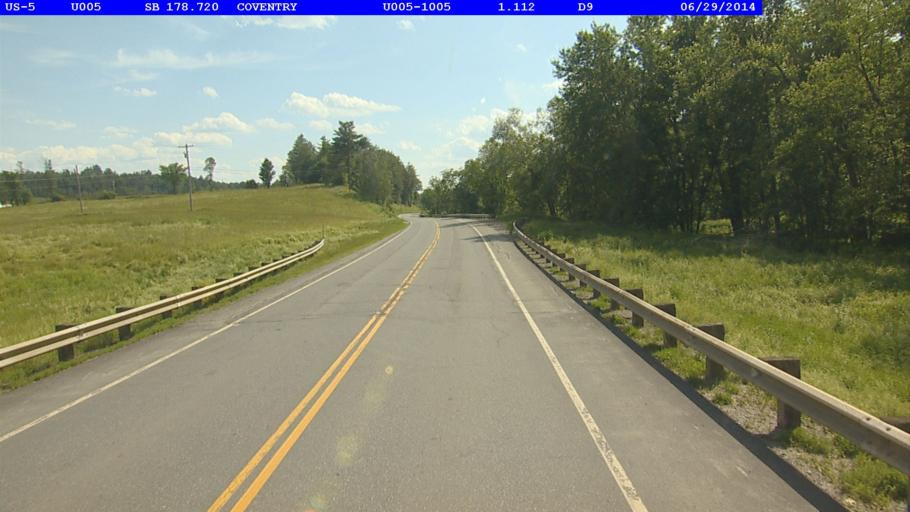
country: US
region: Vermont
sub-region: Orleans County
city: Newport
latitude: 44.8726
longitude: -72.2558
